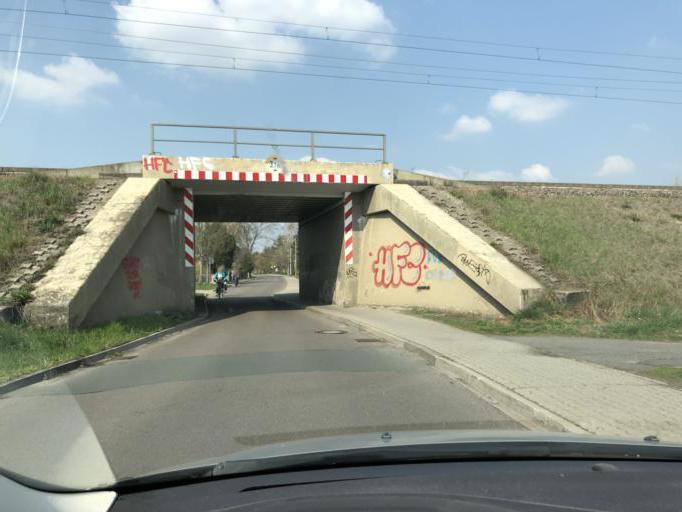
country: DE
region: Saxony-Anhalt
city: Landsberg
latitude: 51.5270
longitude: 12.1532
